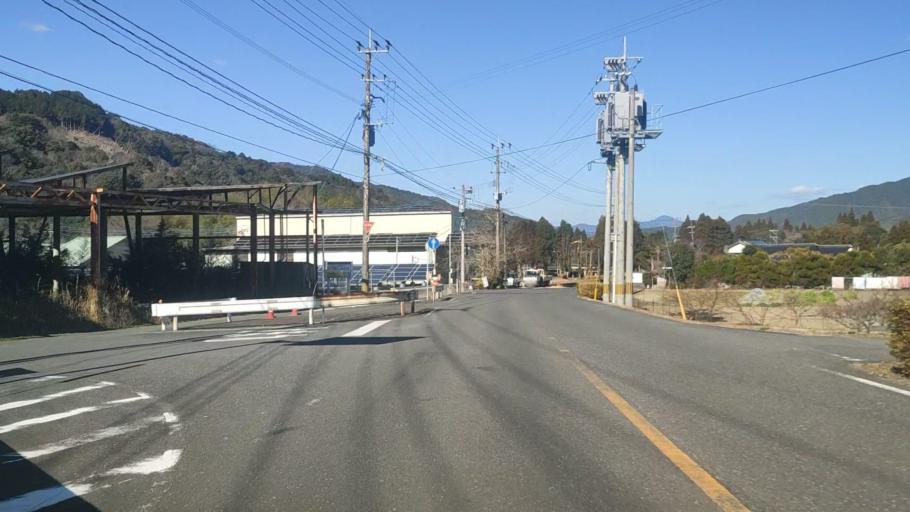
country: JP
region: Oita
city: Saiki
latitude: 32.9019
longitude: 131.9336
